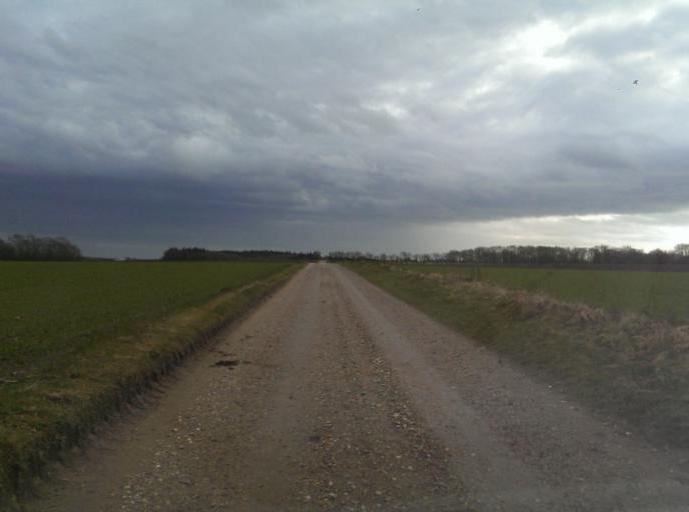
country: DK
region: South Denmark
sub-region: Esbjerg Kommune
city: Tjaereborg
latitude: 55.4873
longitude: 8.5980
